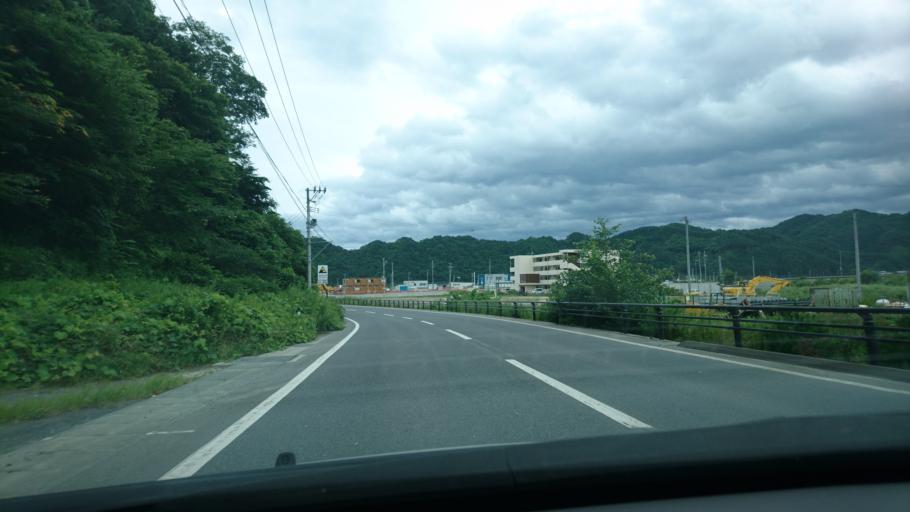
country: JP
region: Iwate
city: Otsuchi
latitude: 39.3343
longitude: 141.8856
